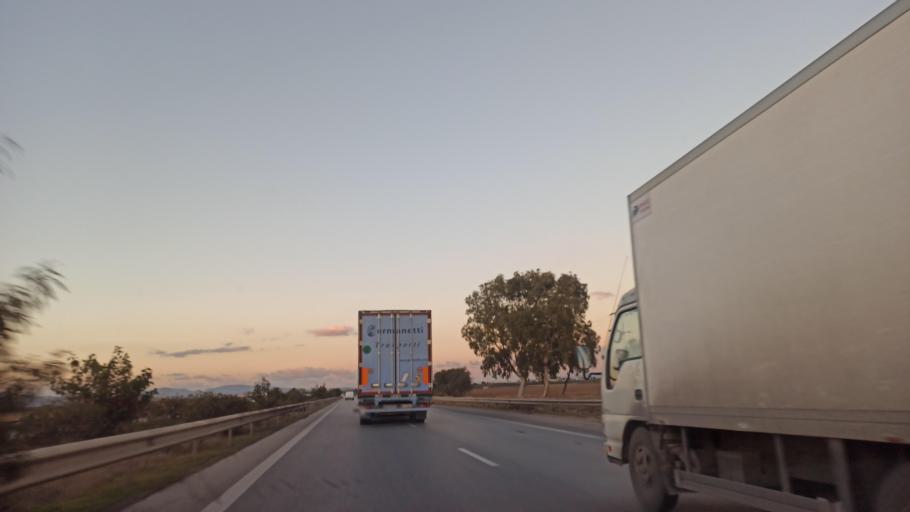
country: TN
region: Nabul
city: Al Hammamat
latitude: 36.2708
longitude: 10.4329
